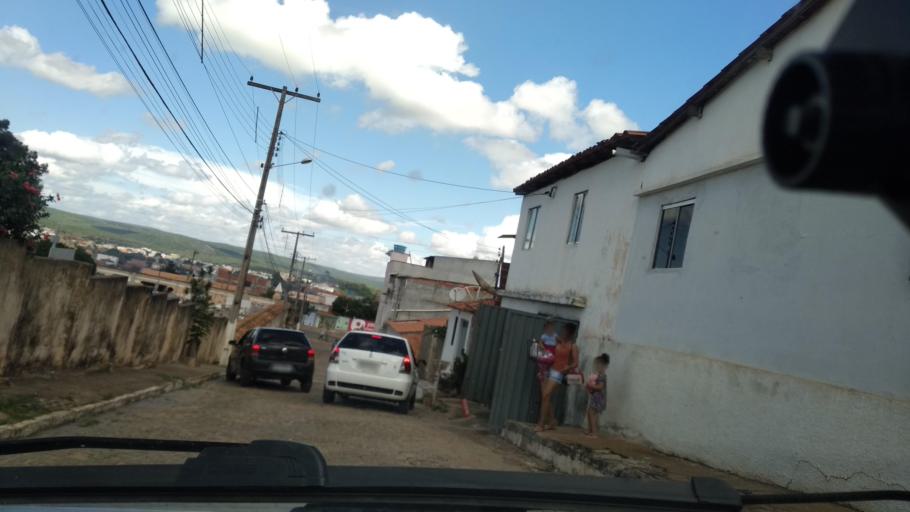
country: BR
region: Bahia
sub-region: Caetite
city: Caetite
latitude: -14.0631
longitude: -42.4852
